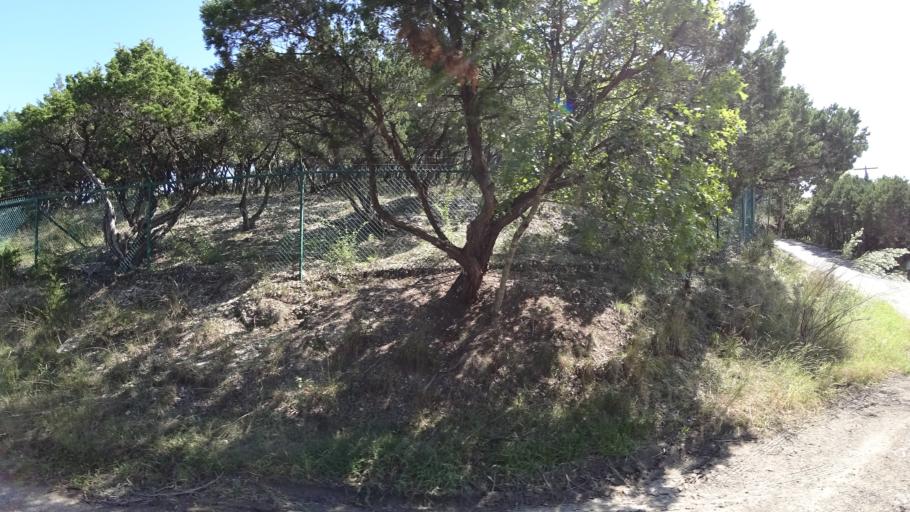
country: US
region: Texas
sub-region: Travis County
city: West Lake Hills
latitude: 30.2973
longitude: -97.8000
